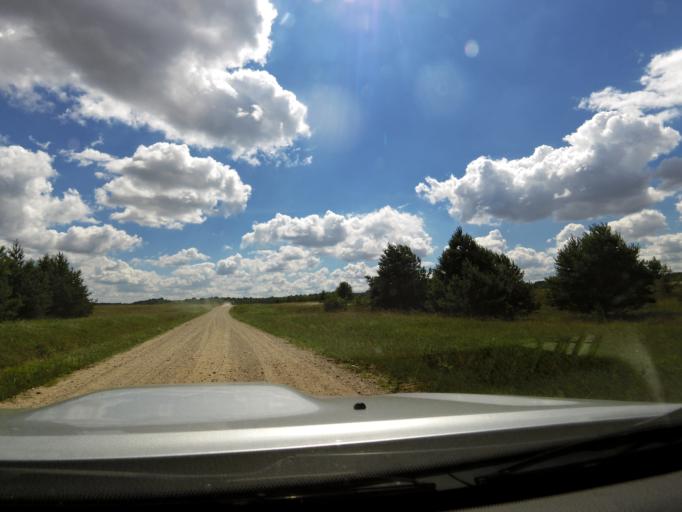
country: LT
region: Vilnius County
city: Elektrenai
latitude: 54.9461
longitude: 24.6732
